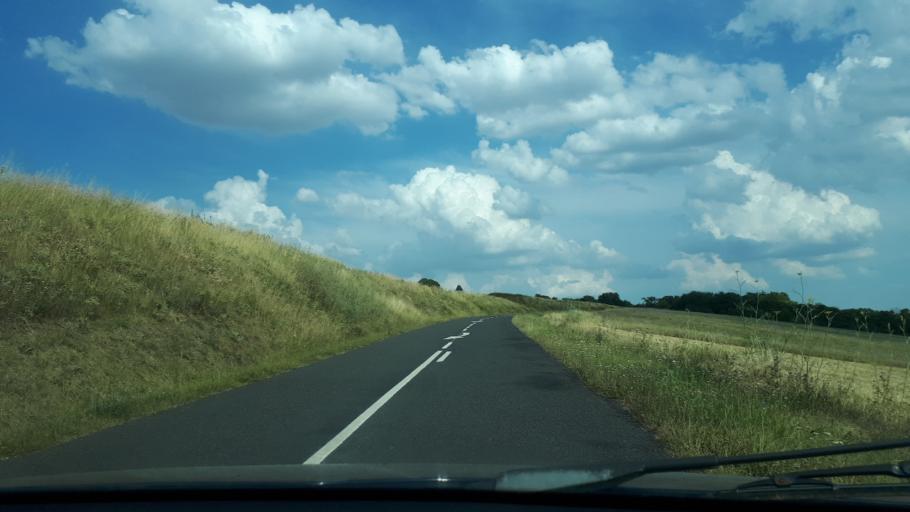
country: FR
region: Pays de la Loire
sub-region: Departement de la Sarthe
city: Besse-sur-Braye
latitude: 47.7790
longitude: 0.7858
